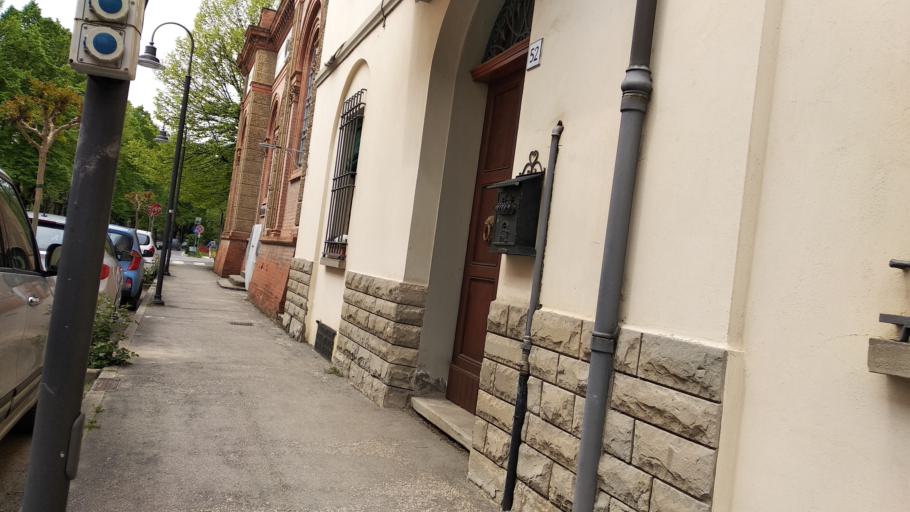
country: IT
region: Emilia-Romagna
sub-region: Provincia di Ravenna
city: Brisighella
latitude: 44.2220
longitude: 11.7695
